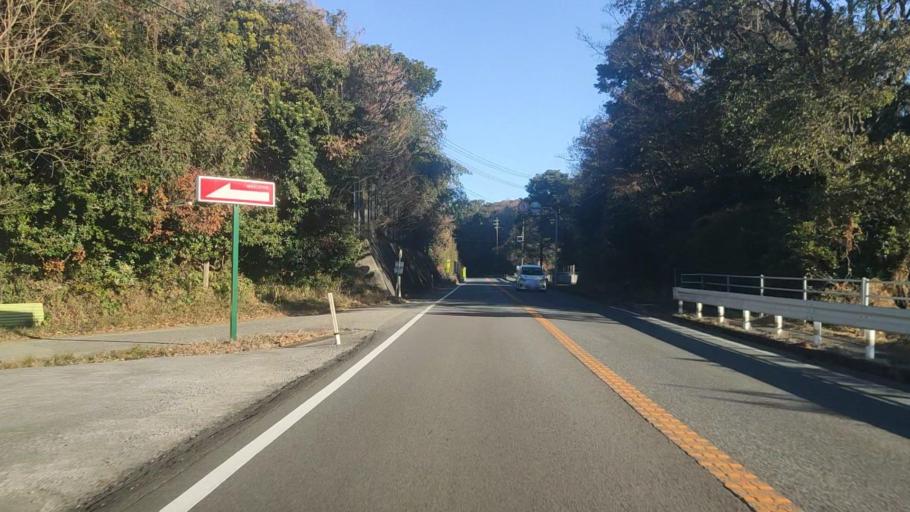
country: JP
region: Miyazaki
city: Nobeoka
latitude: 32.3495
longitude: 131.6228
